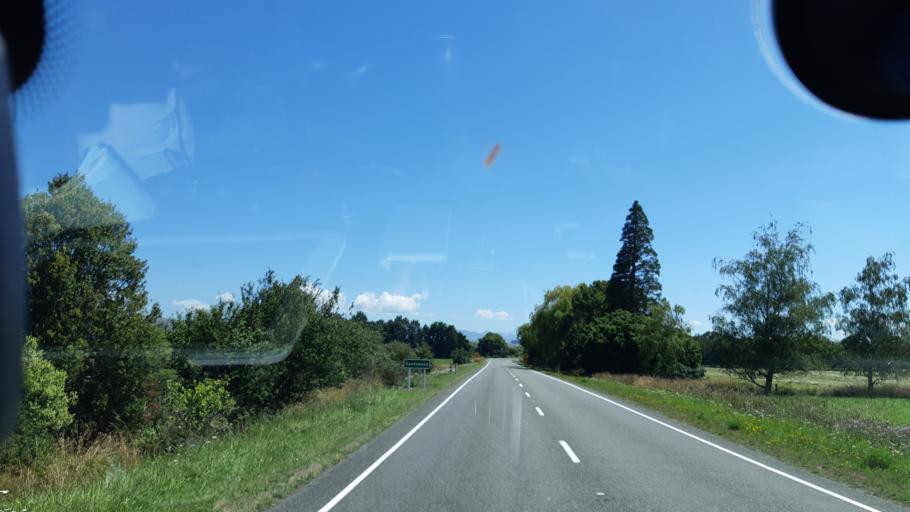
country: NZ
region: Canterbury
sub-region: Kaikoura District
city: Kaikoura
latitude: -42.7432
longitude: 173.2669
